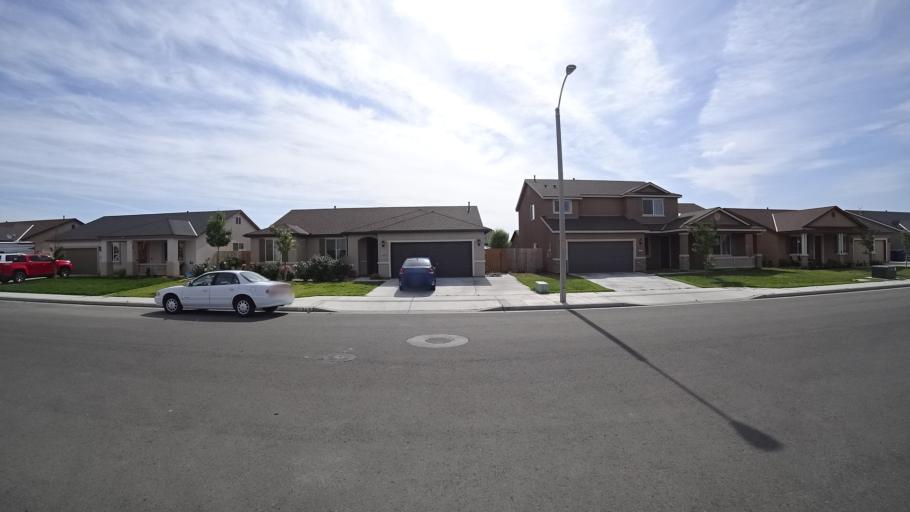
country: US
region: California
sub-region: Kings County
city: Hanford
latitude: 36.3079
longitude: -119.6686
